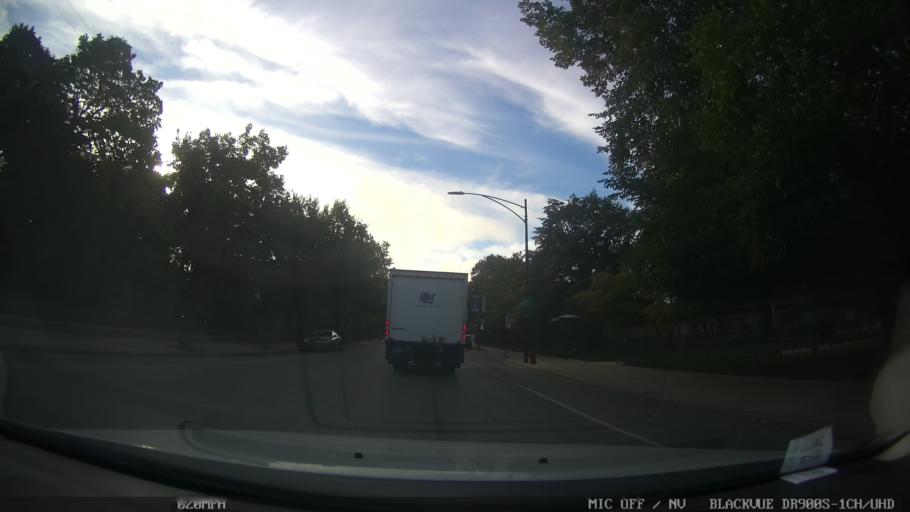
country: US
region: Illinois
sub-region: Cook County
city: Lincolnwood
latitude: 41.9537
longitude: -87.6617
